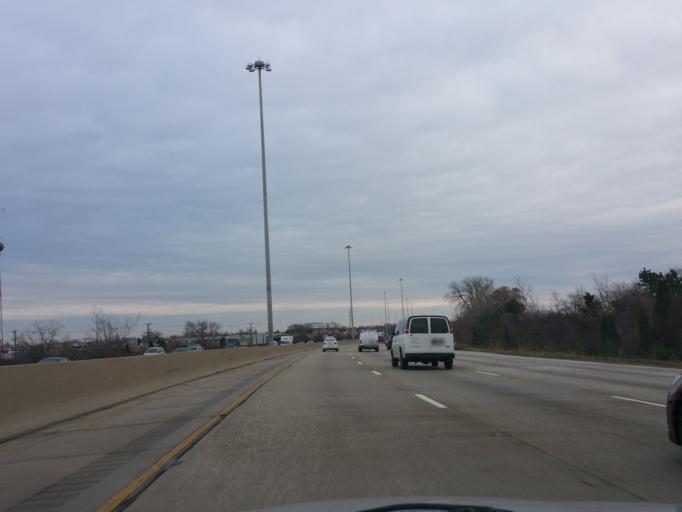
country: US
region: Illinois
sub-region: DuPage County
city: Elmhurst
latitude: 41.9234
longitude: -87.9504
